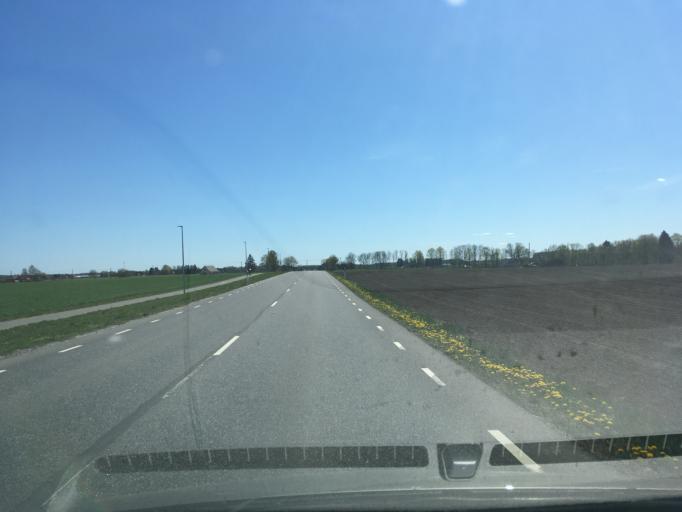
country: EE
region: Harju
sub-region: Maardu linn
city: Maardu
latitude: 59.4432
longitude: 25.0698
